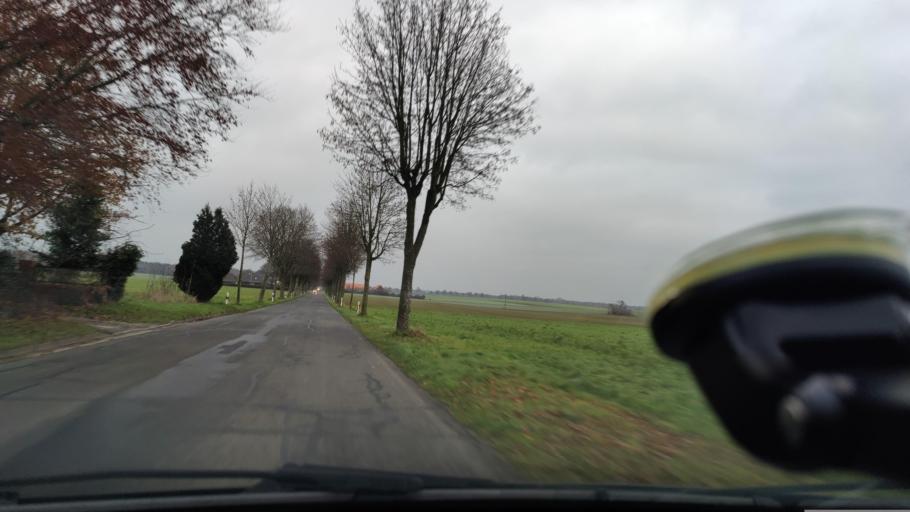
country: DE
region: North Rhine-Westphalia
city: Kalkar
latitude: 51.7307
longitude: 6.2364
